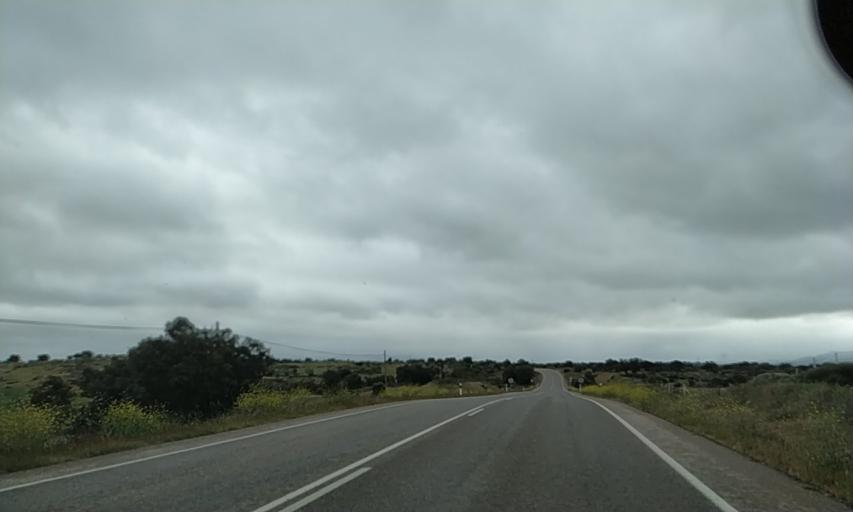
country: ES
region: Extremadura
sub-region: Provincia de Caceres
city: Caceres
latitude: 39.4091
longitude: -6.4167
